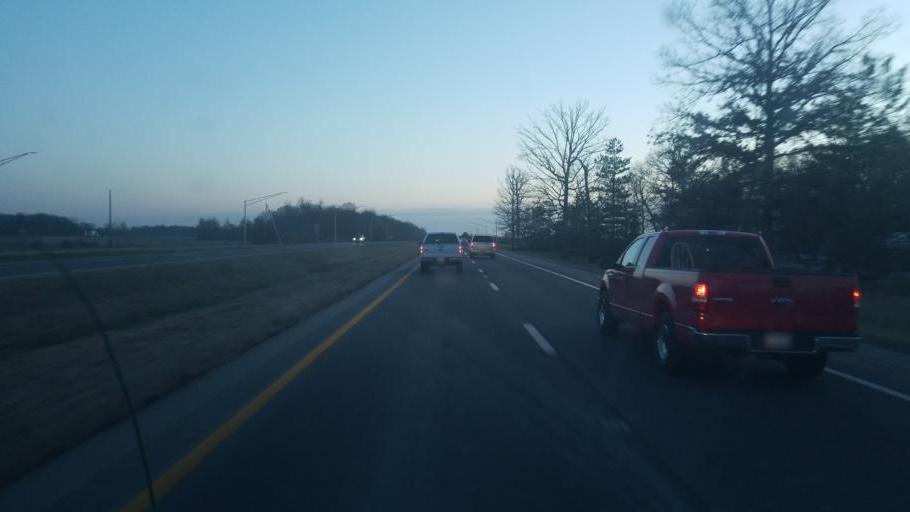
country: US
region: Ohio
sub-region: Marion County
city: Marion
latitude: 40.5274
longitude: -83.0748
